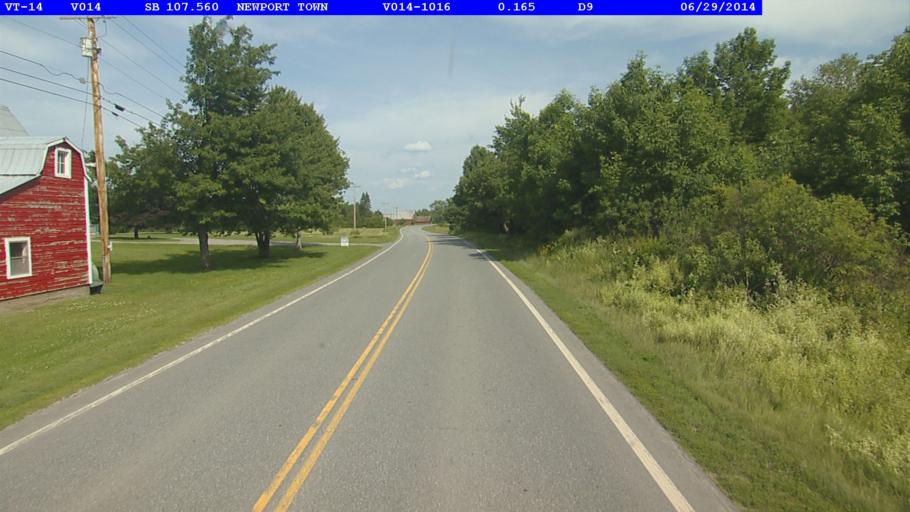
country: US
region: Vermont
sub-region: Orleans County
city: Newport
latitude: 44.9152
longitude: -72.2839
